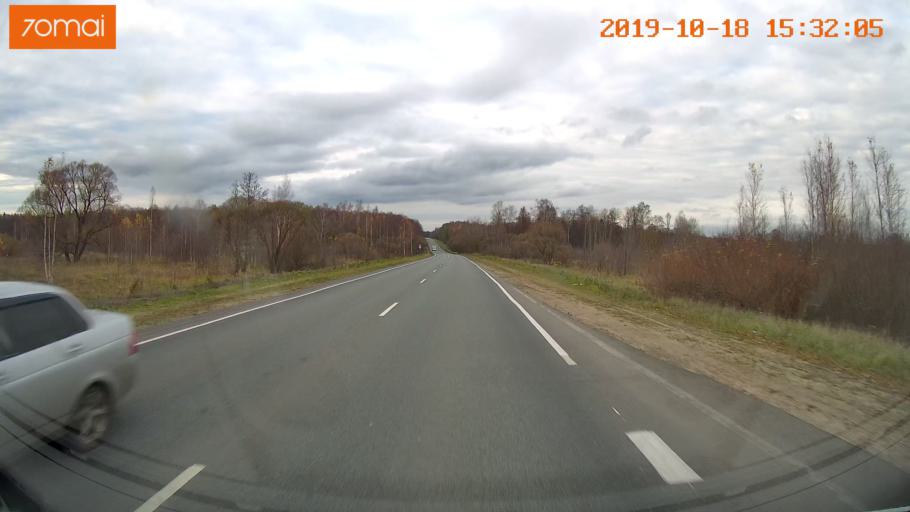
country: RU
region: Vladimir
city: Anopino
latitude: 55.8215
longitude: 40.6594
